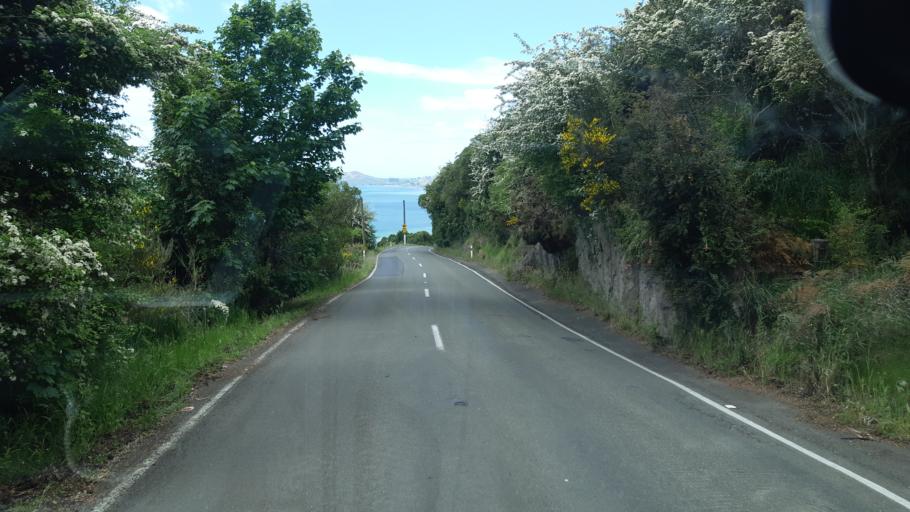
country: NZ
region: Otago
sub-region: Dunedin City
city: Portobello
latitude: -45.8120
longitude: 170.6164
